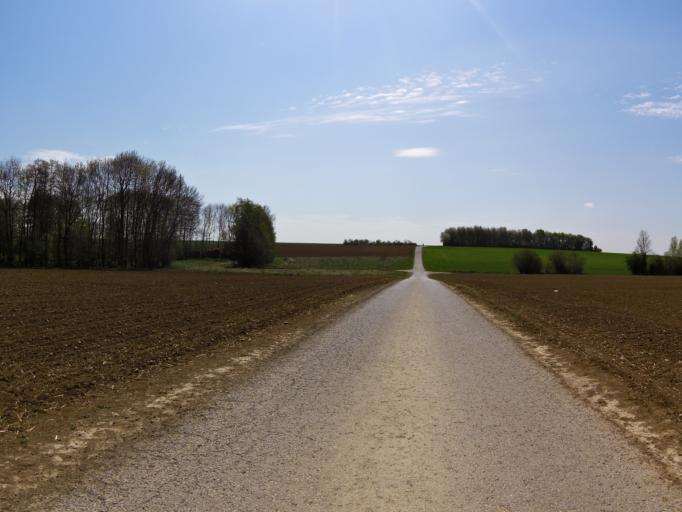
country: DE
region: Bavaria
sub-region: Regierungsbezirk Unterfranken
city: Giebelstadt
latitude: 49.6912
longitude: 9.9628
